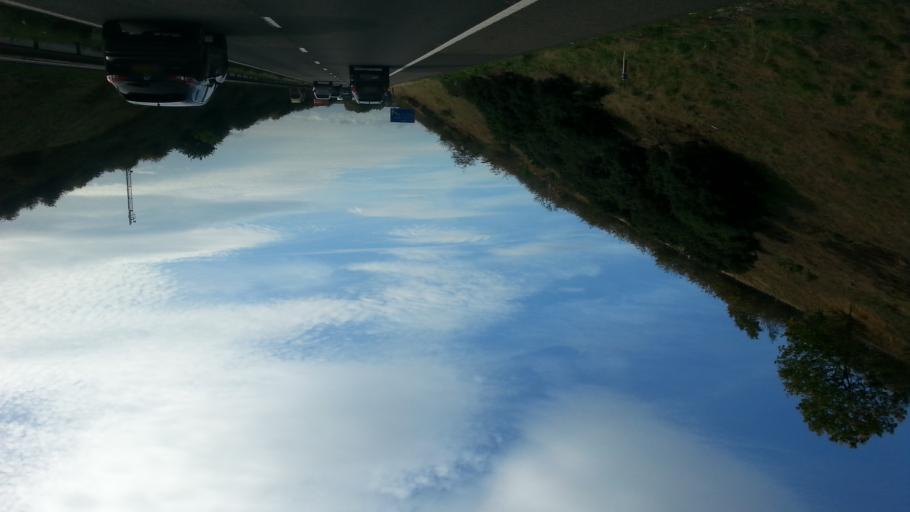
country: GB
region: England
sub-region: Nottinghamshire
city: Bircotes
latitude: 53.4069
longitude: -1.0813
